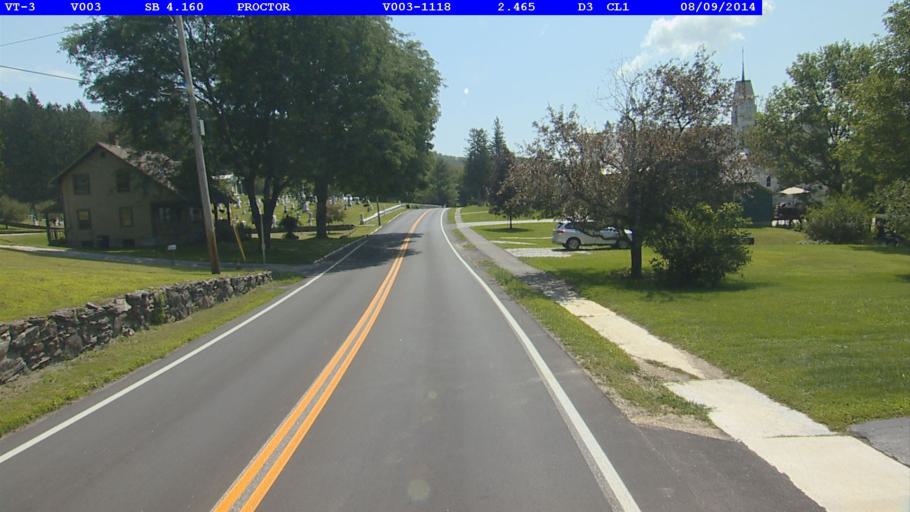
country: US
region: Vermont
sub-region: Rutland County
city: West Rutland
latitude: 43.6591
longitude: -73.0322
